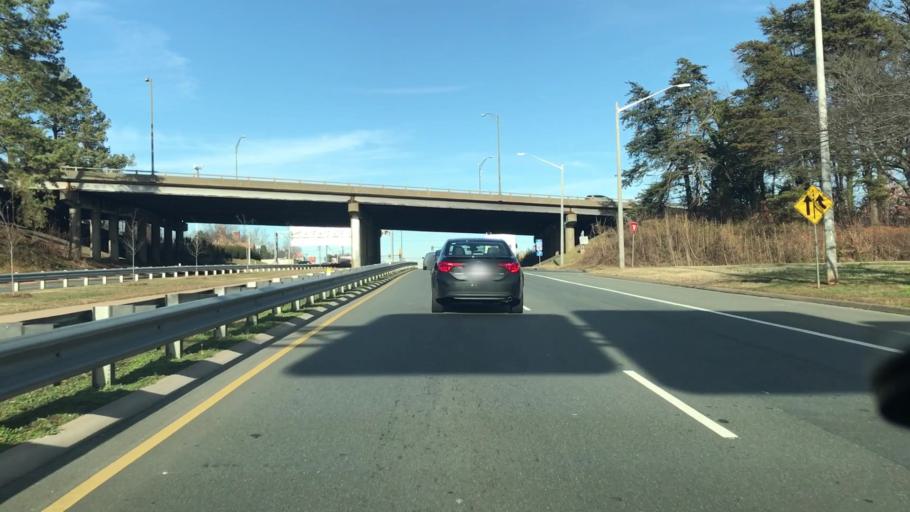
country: US
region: Virginia
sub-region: City of Charlottesville
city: Charlottesville
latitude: 38.0565
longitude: -78.4959
